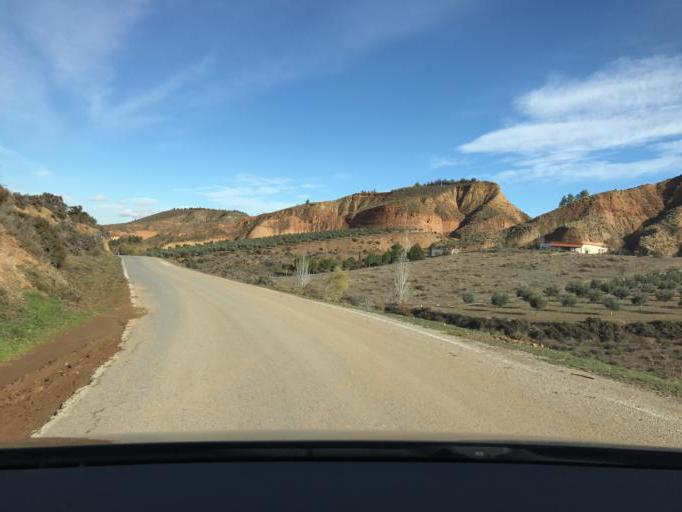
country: ES
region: Andalusia
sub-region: Provincia de Granada
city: Marchal
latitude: 37.2945
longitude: -3.2176
